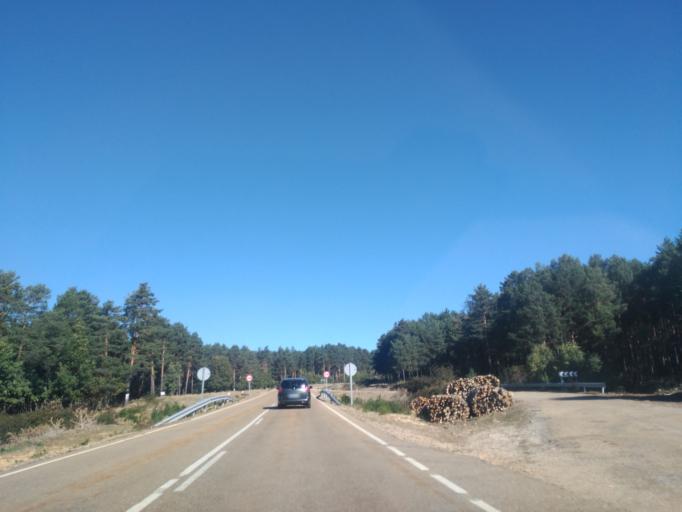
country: ES
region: Castille and Leon
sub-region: Provincia de Soria
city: Vinuesa
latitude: 41.9478
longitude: -2.7734
